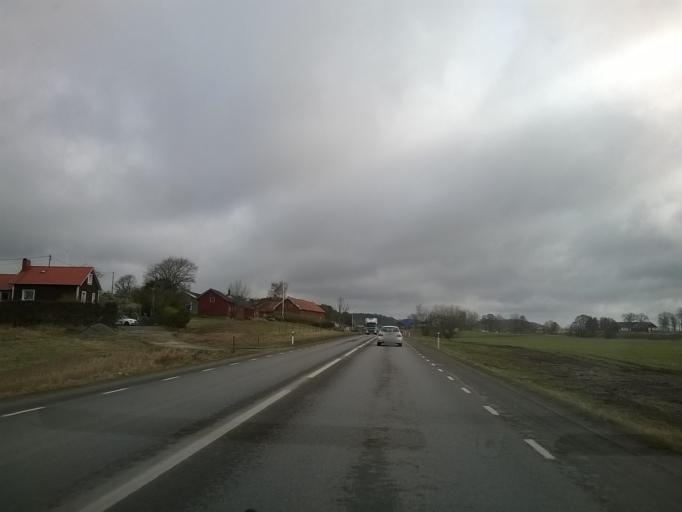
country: SE
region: Halland
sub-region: Varbergs Kommun
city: Varberg
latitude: 57.1309
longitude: 12.3176
